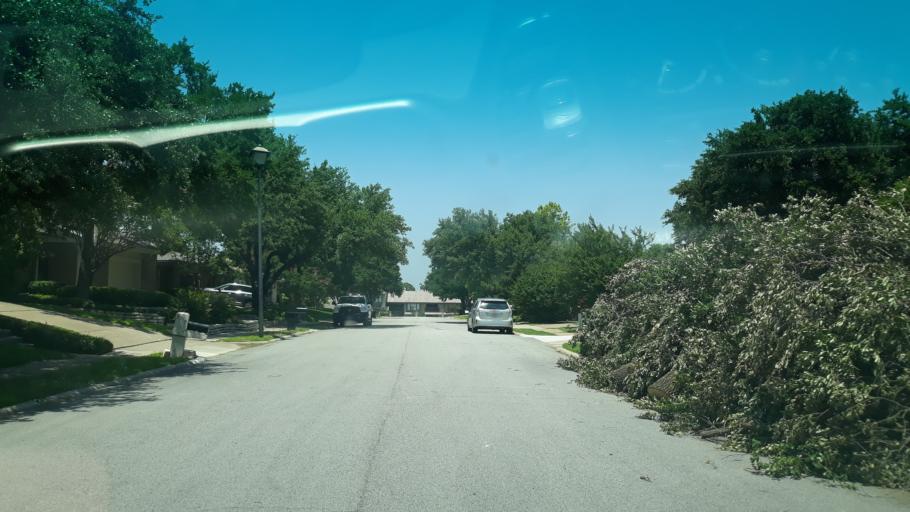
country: US
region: Texas
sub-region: Dallas County
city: Irving
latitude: 32.8575
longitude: -96.9538
